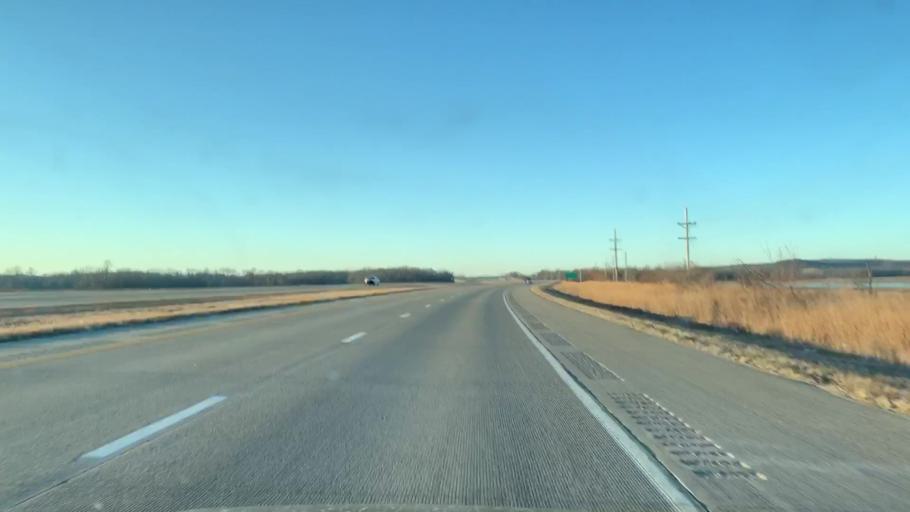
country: US
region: Kansas
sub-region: Linn County
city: Pleasanton
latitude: 38.2328
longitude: -94.6925
